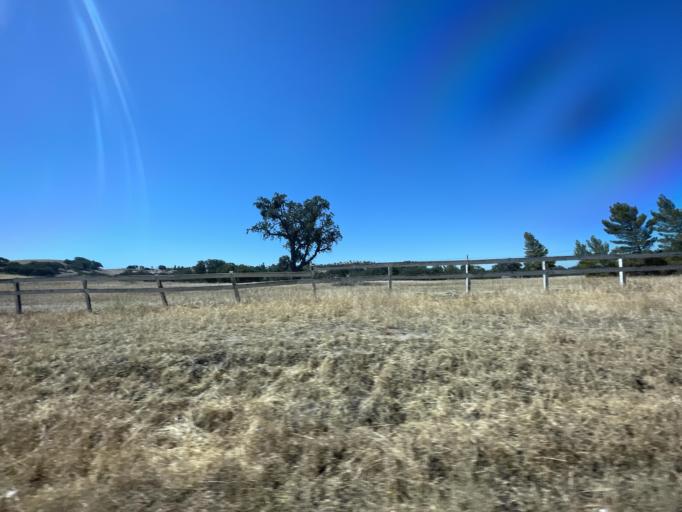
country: US
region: California
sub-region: San Luis Obispo County
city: Paso Robles
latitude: 35.6300
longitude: -120.6074
